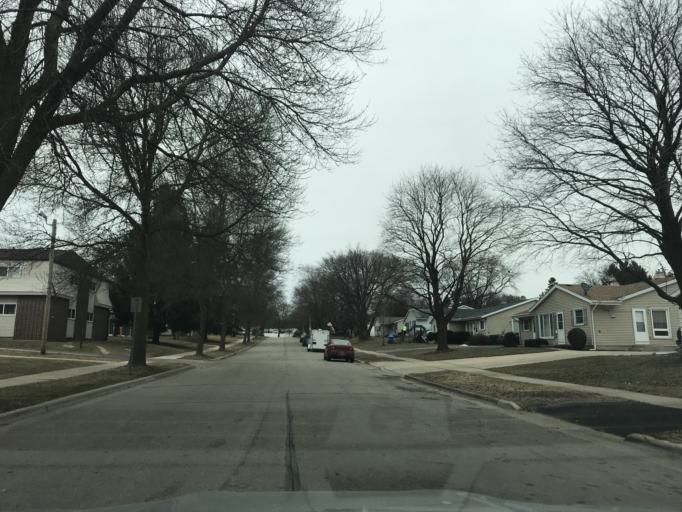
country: US
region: Wisconsin
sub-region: Dane County
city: Monona
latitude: 43.0872
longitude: -89.3057
